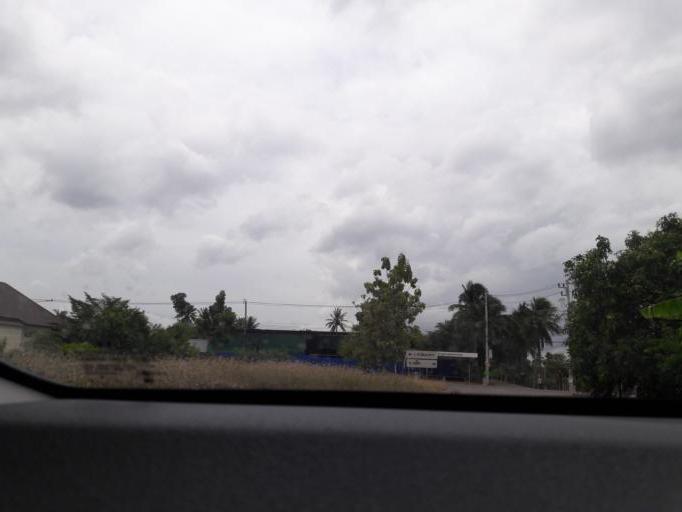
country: TH
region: Ratchaburi
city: Damnoen Saduak
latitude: 13.5713
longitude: 99.9803
